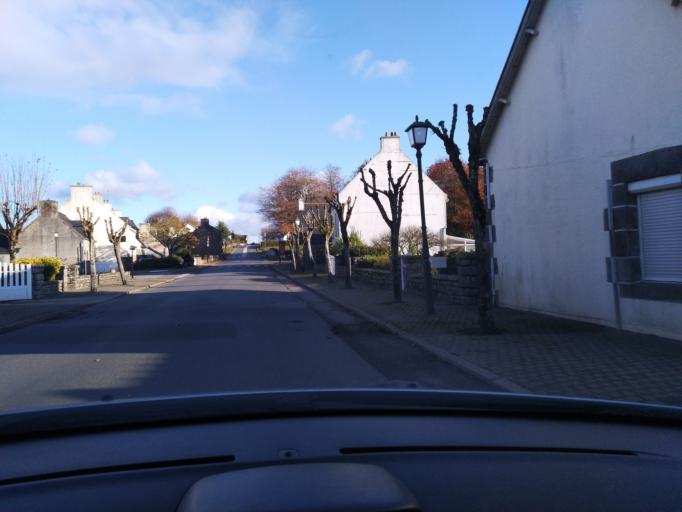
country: FR
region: Brittany
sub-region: Departement du Finistere
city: Guerlesquin
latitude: 48.5171
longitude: -3.5843
